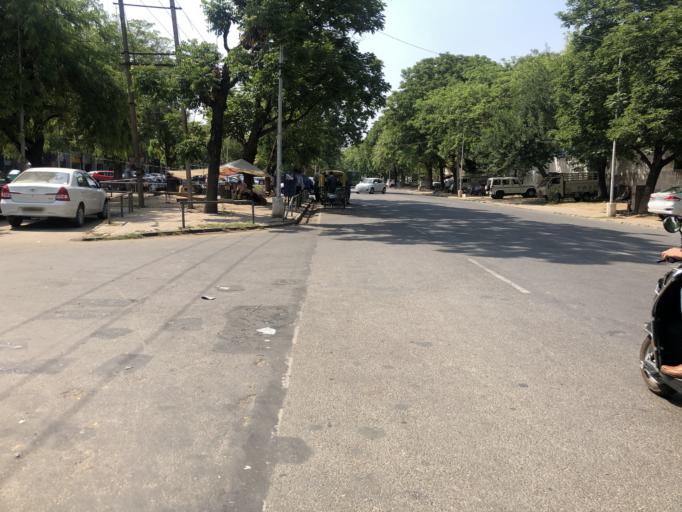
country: IN
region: Chandigarh
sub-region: Chandigarh
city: Chandigarh
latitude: 30.6941
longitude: 76.7714
